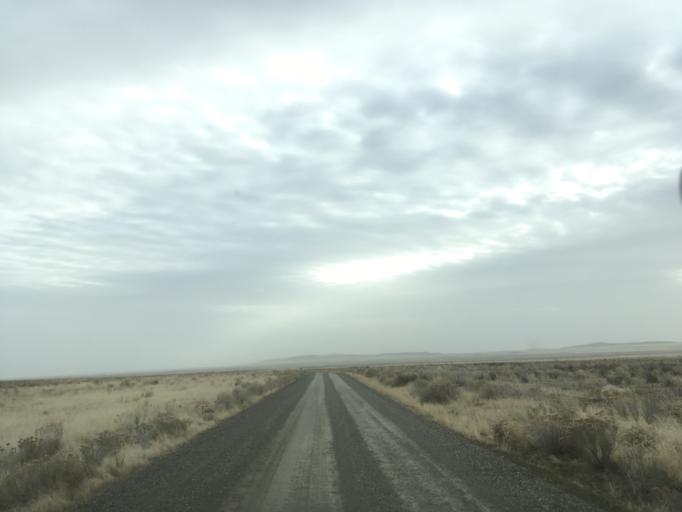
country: US
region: Utah
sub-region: Box Elder County
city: Tremonton
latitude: 41.5342
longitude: -112.6208
